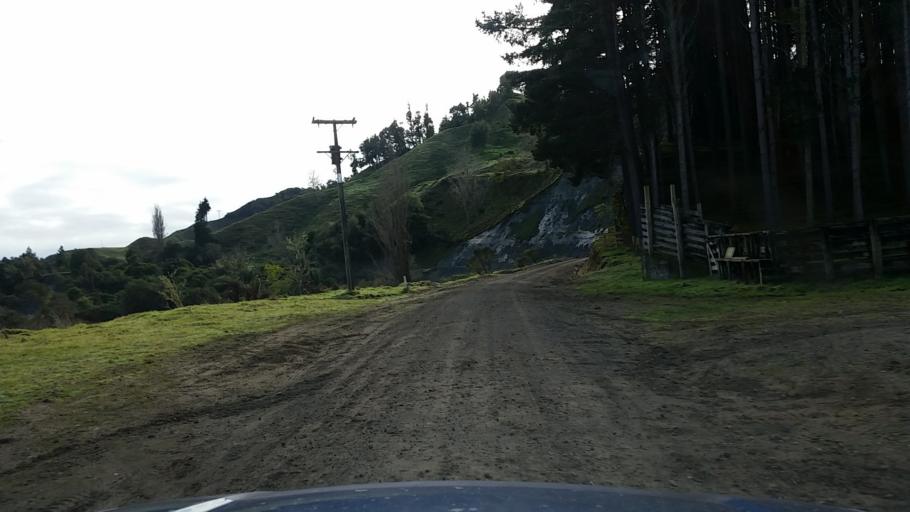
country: NZ
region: Taranaki
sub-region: New Plymouth District
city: Waitara
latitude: -39.1098
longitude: 174.8481
